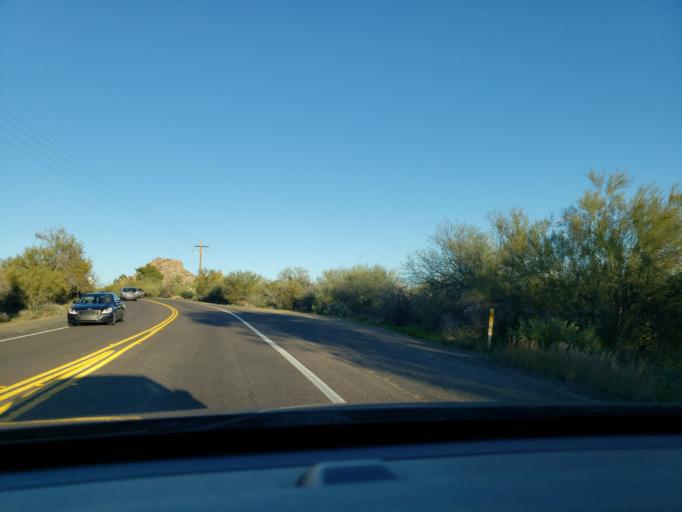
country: US
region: Arizona
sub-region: Maricopa County
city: Carefree
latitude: 33.7992
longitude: -111.9375
